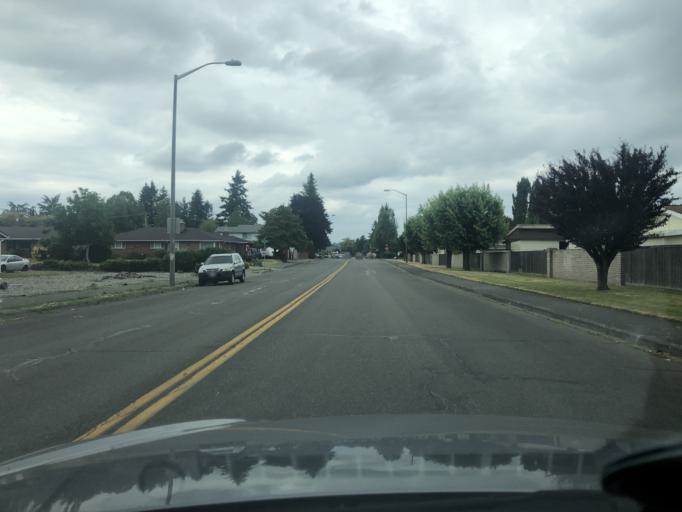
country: US
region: Washington
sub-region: King County
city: Auburn
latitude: 47.3251
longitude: -122.2141
